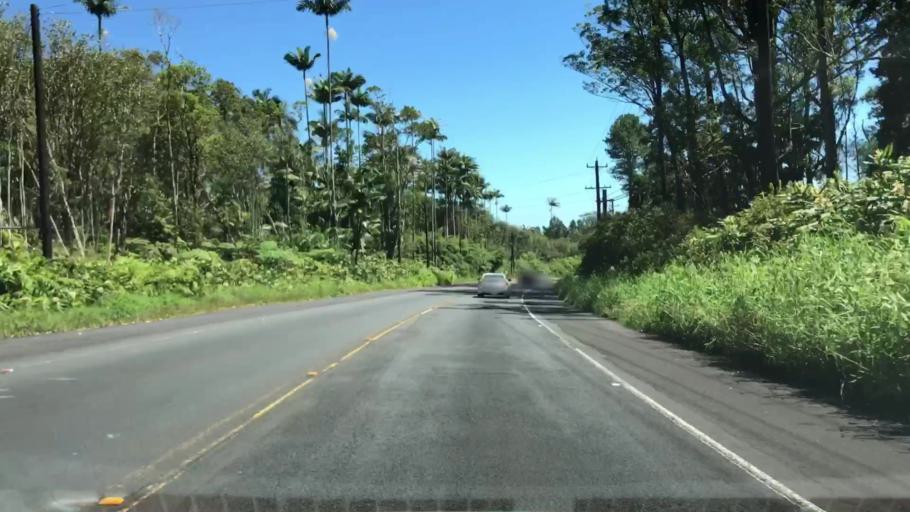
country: US
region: Hawaii
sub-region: Hawaii County
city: Mountain View
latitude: 19.5280
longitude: -155.1340
